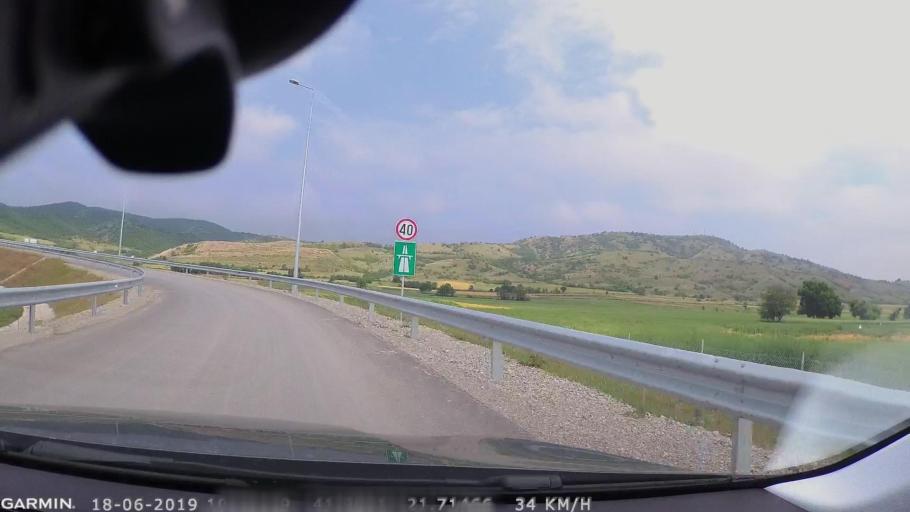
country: MK
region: Petrovec
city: Sredno Konjare
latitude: 41.9441
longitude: 21.8078
